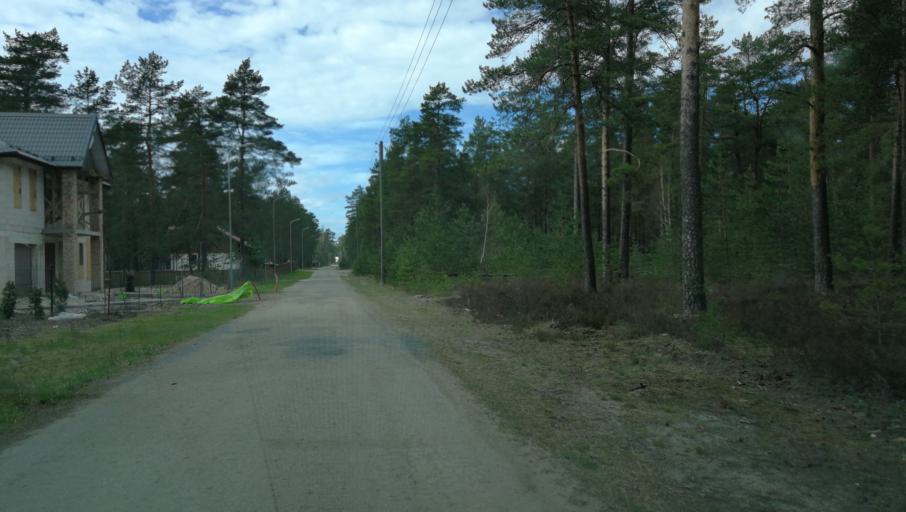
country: LV
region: Garkalne
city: Garkalne
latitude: 57.0369
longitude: 24.4438
